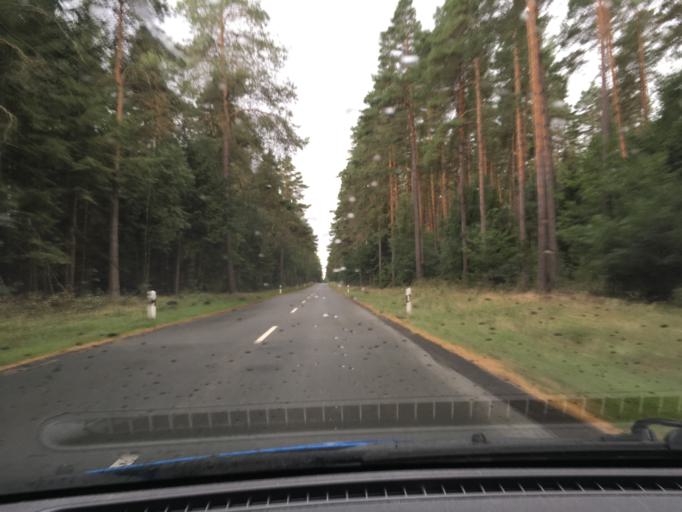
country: DE
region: Lower Saxony
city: Wietzendorf
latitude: 52.8861
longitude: 9.9979
